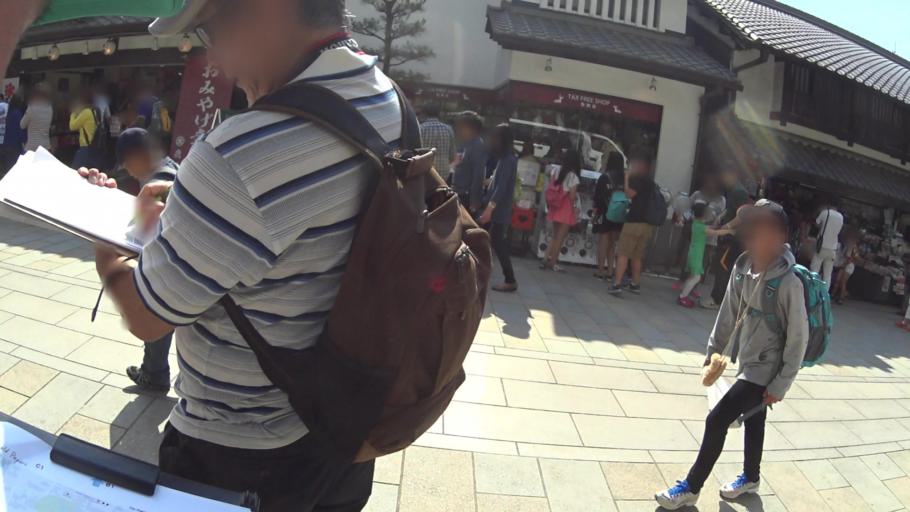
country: JP
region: Nara
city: Nara-shi
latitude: 34.6839
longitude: 135.8399
